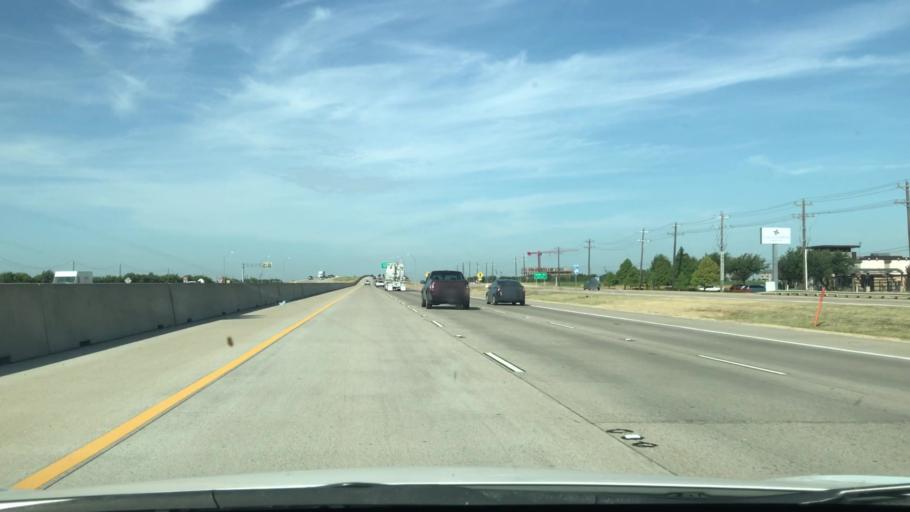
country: US
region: Texas
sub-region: Collin County
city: Allen
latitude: 33.1371
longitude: -96.6996
